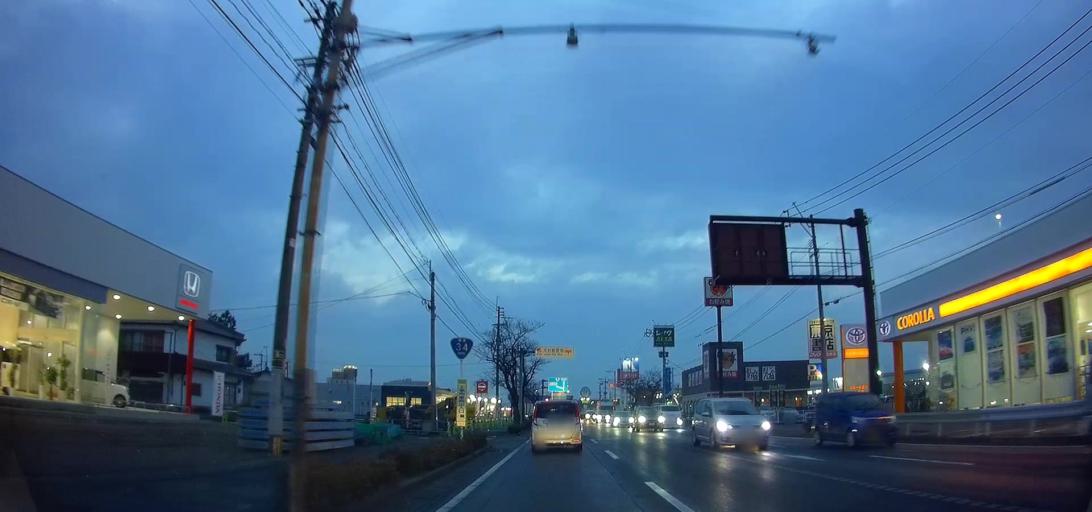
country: JP
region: Nagasaki
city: Omura
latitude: 32.9104
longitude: 129.9529
